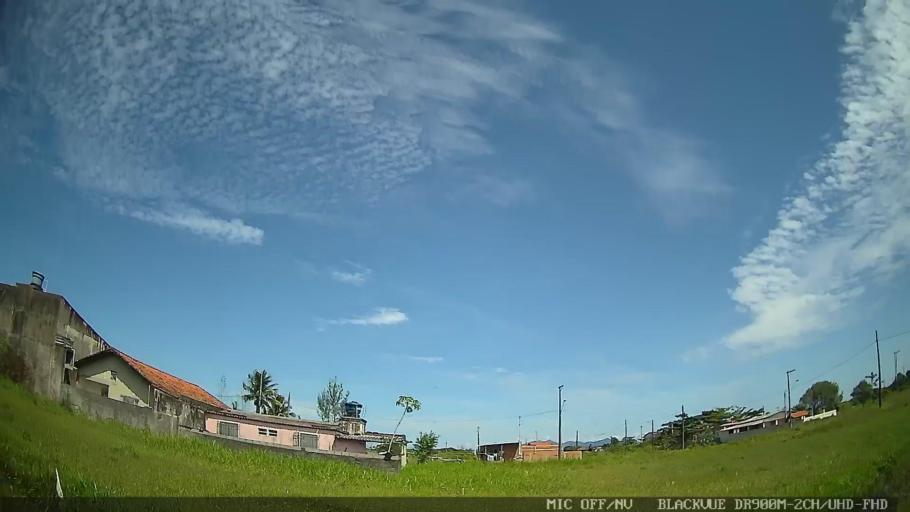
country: BR
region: Sao Paulo
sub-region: Iguape
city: Iguape
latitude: -24.8073
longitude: -47.6402
